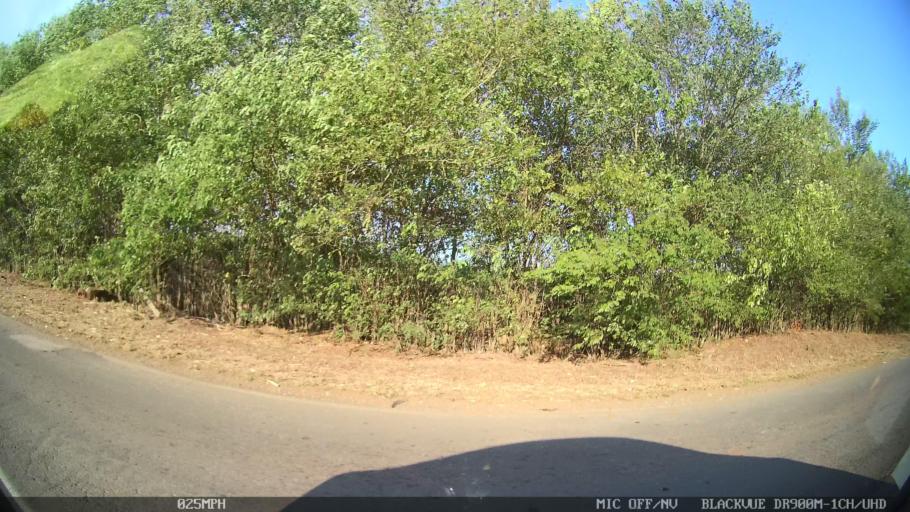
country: BR
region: Sao Paulo
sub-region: Piracicaba
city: Piracicaba
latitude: -22.6958
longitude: -47.6006
